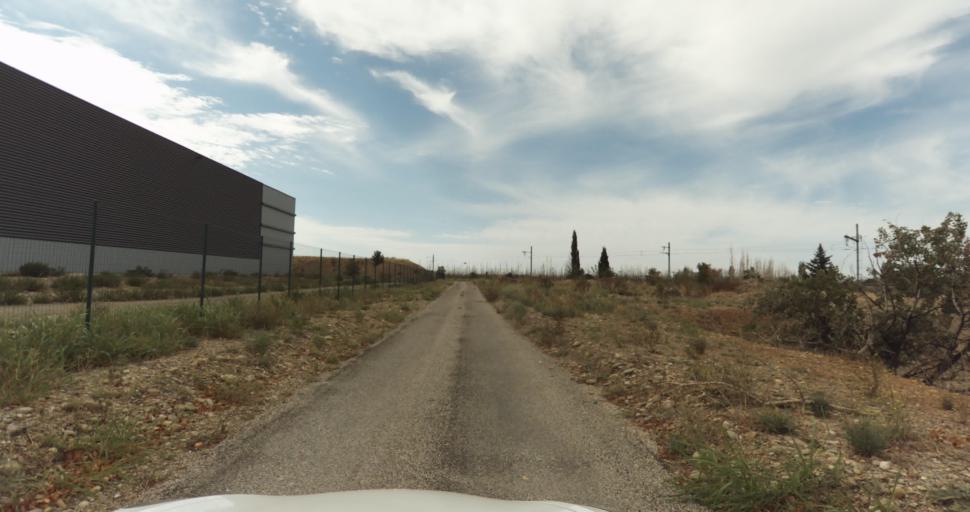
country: FR
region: Provence-Alpes-Cote d'Azur
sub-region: Departement des Bouches-du-Rhone
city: Miramas
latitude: 43.6020
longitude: 4.9895
